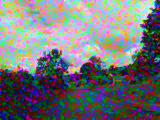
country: IE
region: Ulster
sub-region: County Donegal
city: Letterkenny
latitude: 55.0056
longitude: -7.8193
